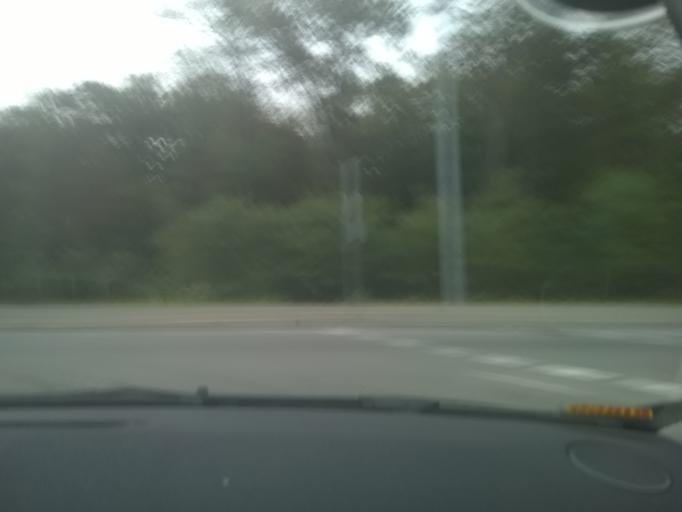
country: HR
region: Zagrebacka
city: Brdovec
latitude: 45.8776
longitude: 15.8014
